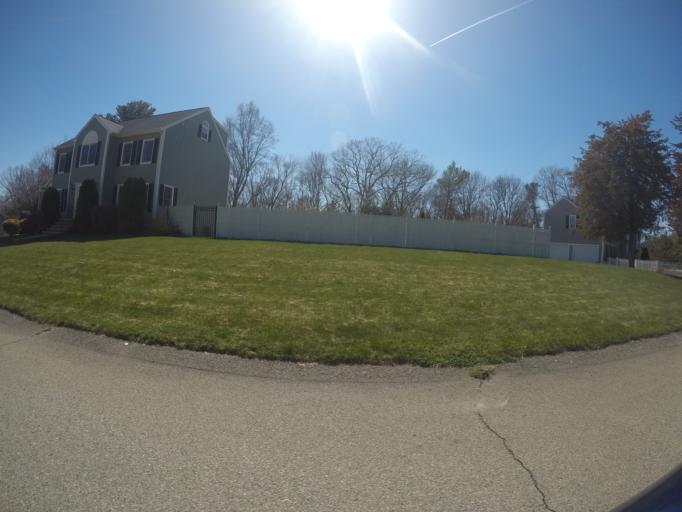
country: US
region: Massachusetts
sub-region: Norfolk County
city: Stoughton
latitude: 42.0855
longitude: -71.0938
